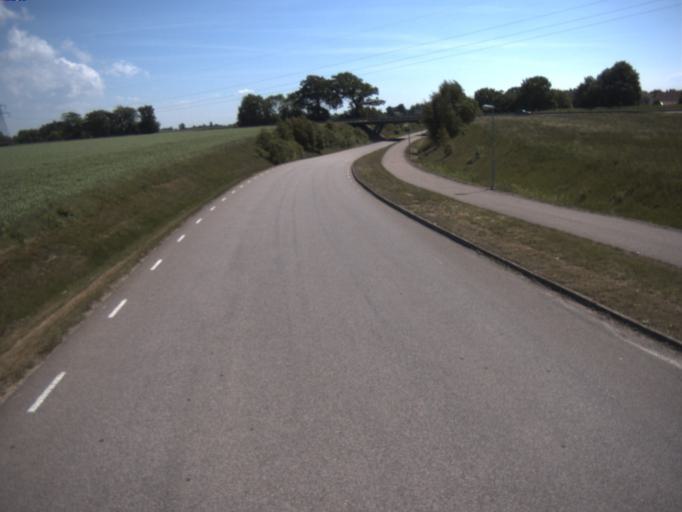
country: SE
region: Skane
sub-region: Helsingborg
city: Barslov
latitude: 56.0159
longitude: 12.8080
